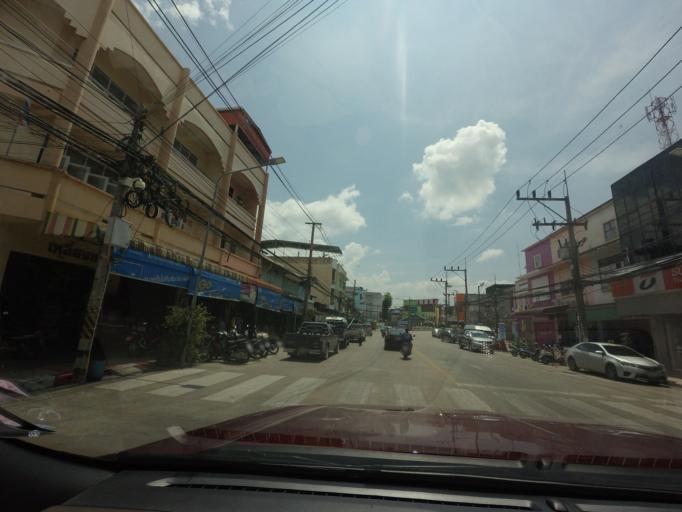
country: TH
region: Yala
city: Betong
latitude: 5.7734
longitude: 101.0716
